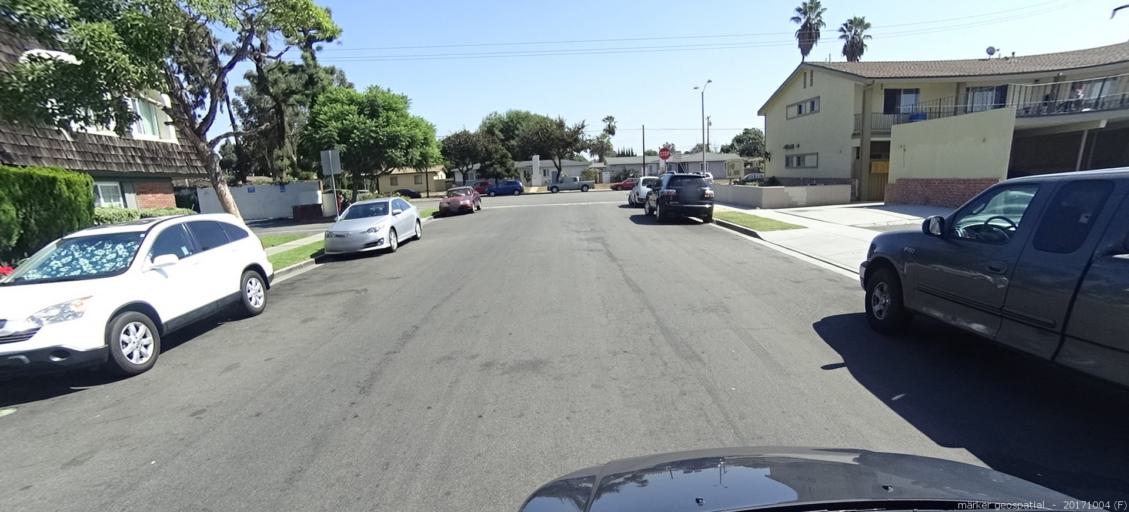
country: US
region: California
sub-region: Orange County
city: Garden Grove
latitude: 33.7999
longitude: -117.9420
